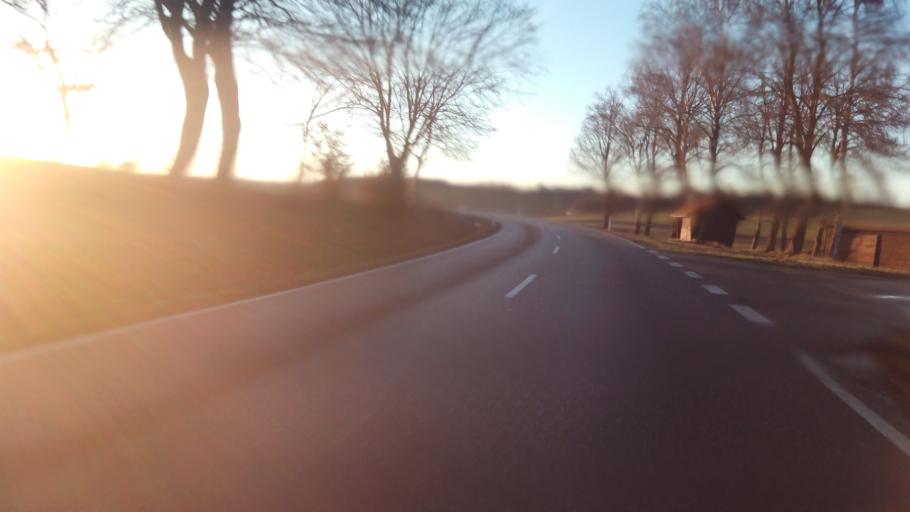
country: DE
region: Baden-Wuerttemberg
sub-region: Tuebingen Region
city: Erbach
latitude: 48.3269
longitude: 9.8707
